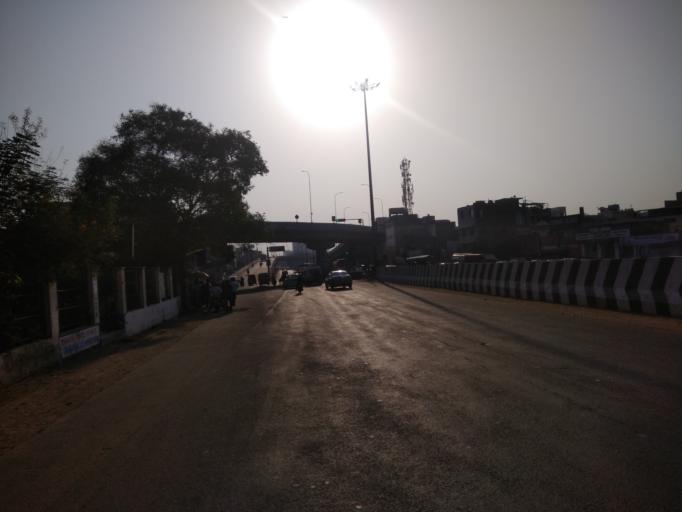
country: IN
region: Tamil Nadu
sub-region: Chennai
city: Chetput
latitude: 13.0741
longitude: 80.2214
